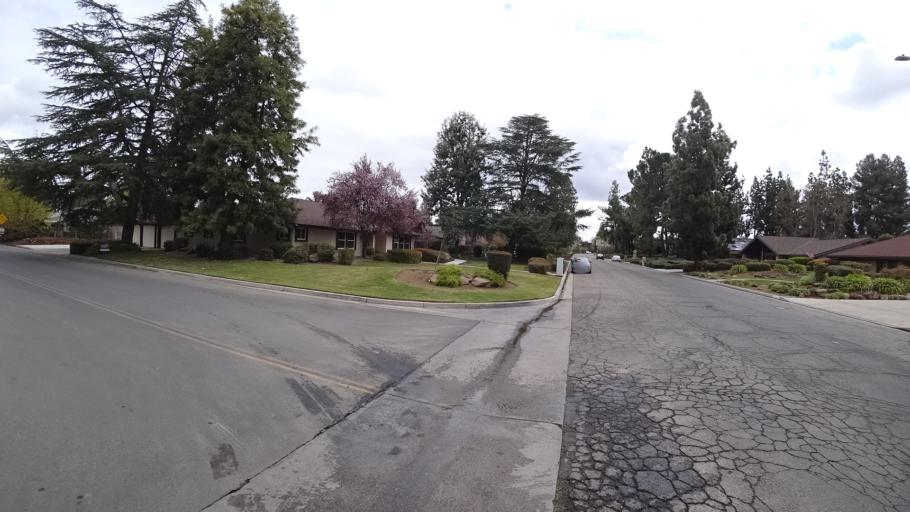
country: US
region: California
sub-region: Fresno County
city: Fresno
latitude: 36.8451
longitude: -119.8186
